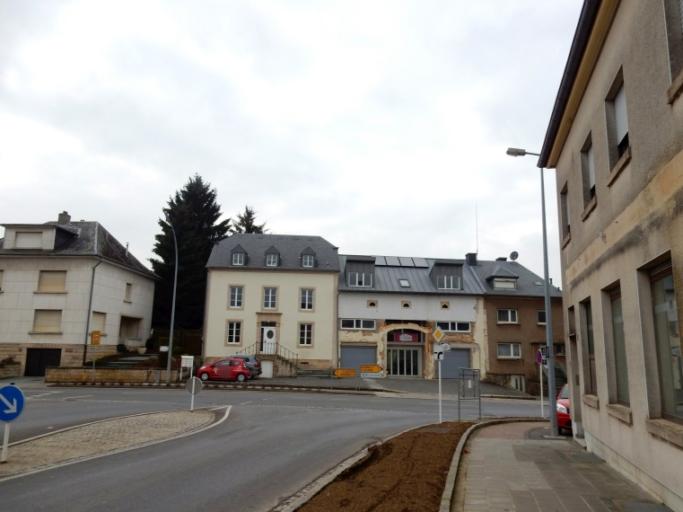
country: LU
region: Luxembourg
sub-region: Canton d'Esch-sur-Alzette
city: Mondercange
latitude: 49.5317
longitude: 5.9868
